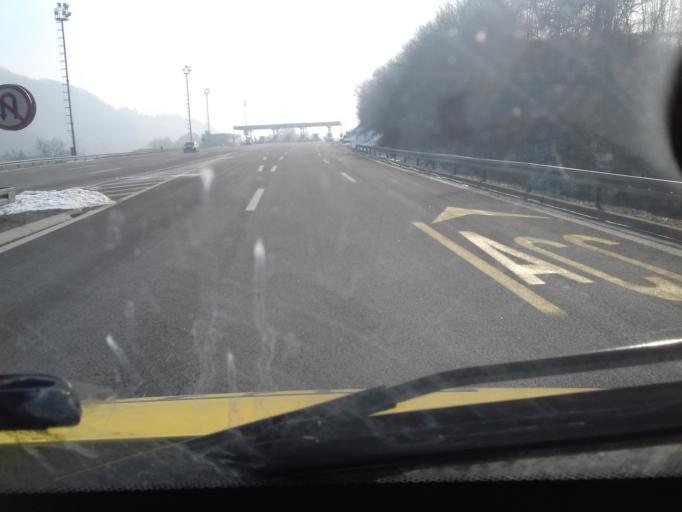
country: BA
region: Federation of Bosnia and Herzegovina
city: Vogosca
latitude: 43.9132
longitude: 18.3194
